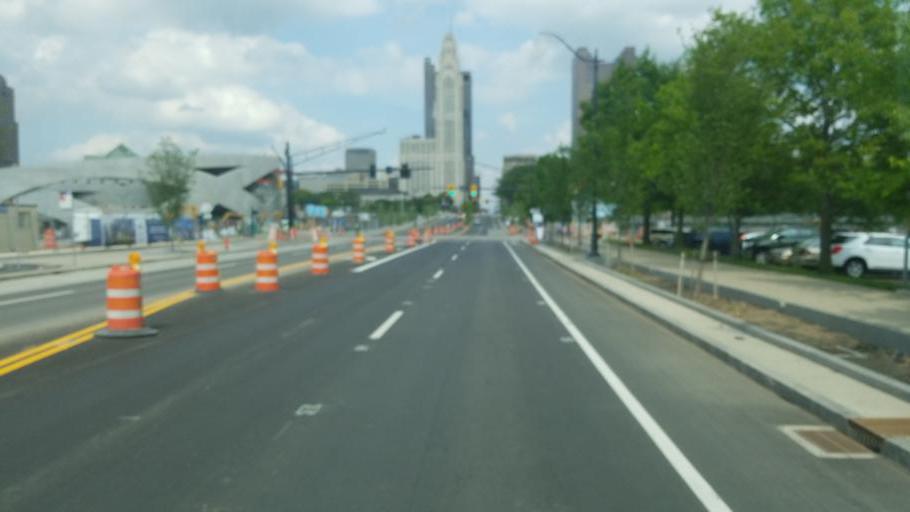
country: US
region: Ohio
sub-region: Franklin County
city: Columbus
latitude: 39.9611
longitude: -83.0098
